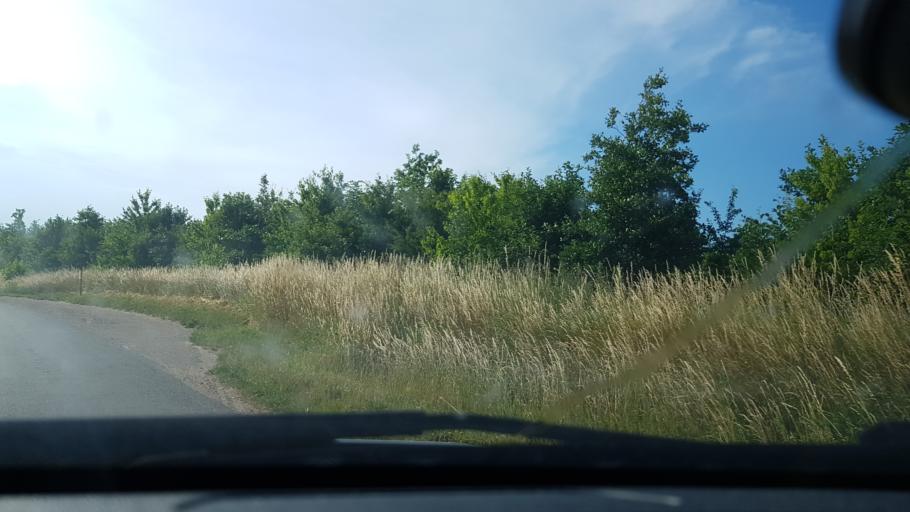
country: DK
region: Zealand
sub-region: Odsherred Kommune
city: Hojby
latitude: 55.8980
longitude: 11.6171
